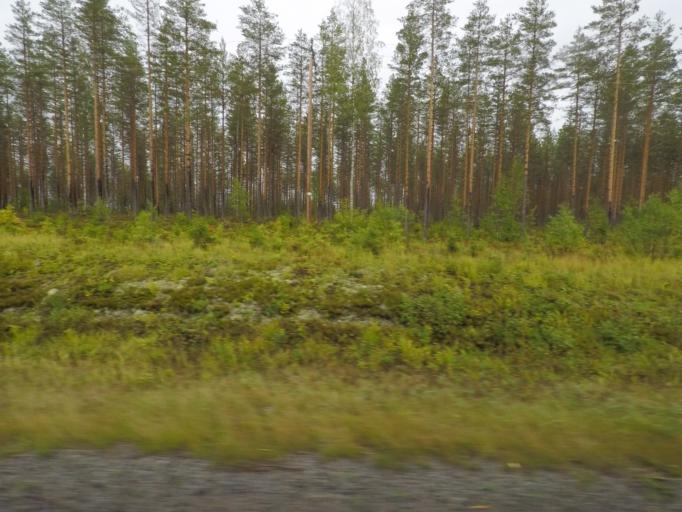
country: FI
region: Southern Savonia
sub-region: Pieksaemaeki
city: Juva
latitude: 61.9587
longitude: 27.8050
